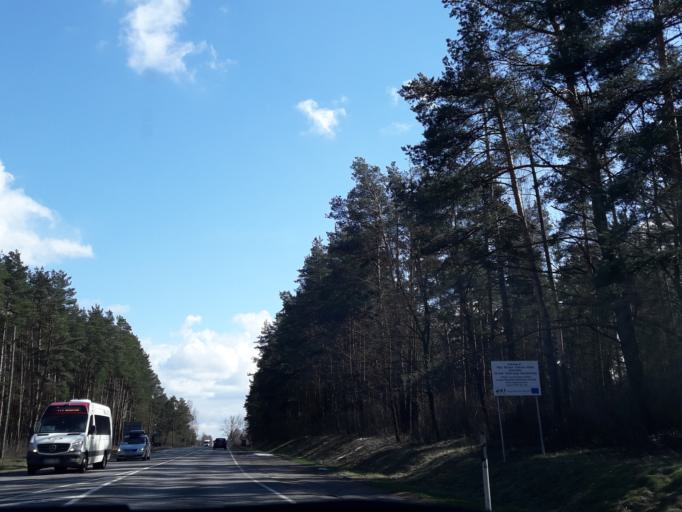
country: LV
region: Kekava
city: Balozi
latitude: 56.8835
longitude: 24.1567
